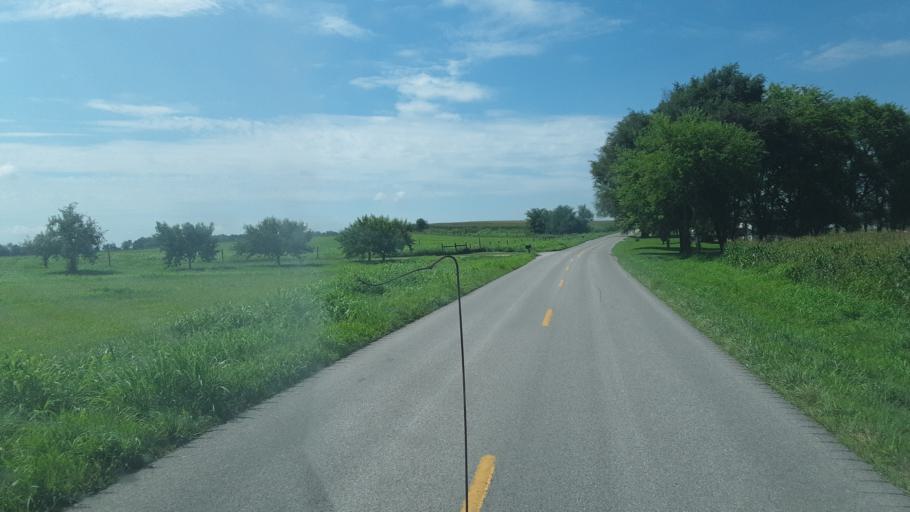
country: US
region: Kentucky
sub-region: Todd County
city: Elkton
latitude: 36.8079
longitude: -87.3150
